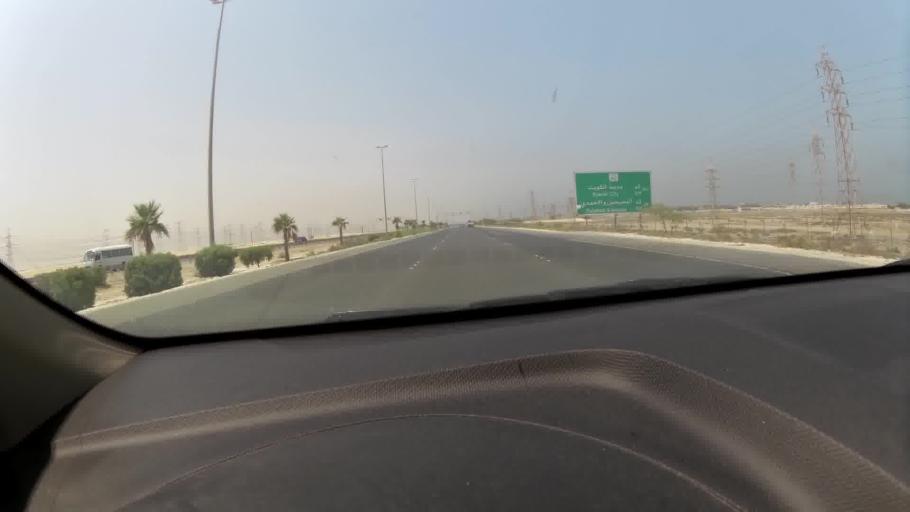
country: KW
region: Al Ahmadi
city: Al Fahahil
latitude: 28.8947
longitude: 48.2221
